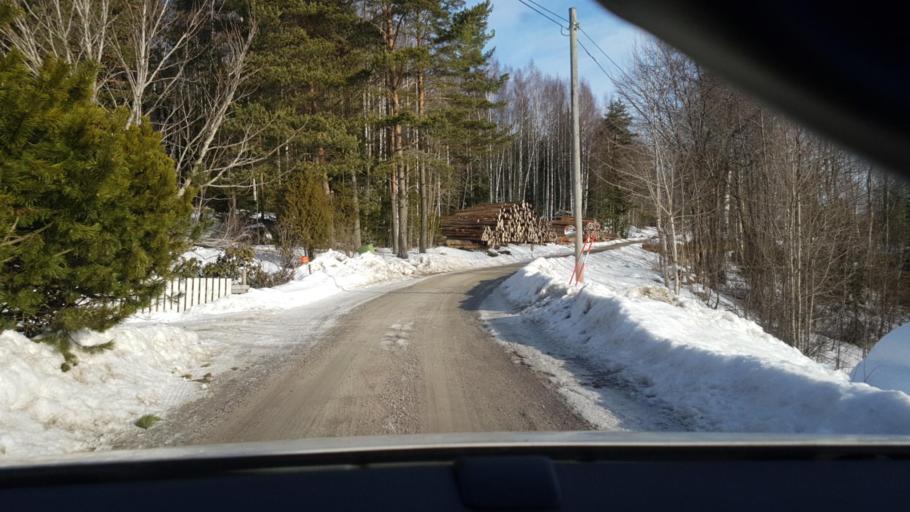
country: SE
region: Vaermland
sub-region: Eda Kommun
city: Amotfors
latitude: 59.7342
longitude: 12.2782
